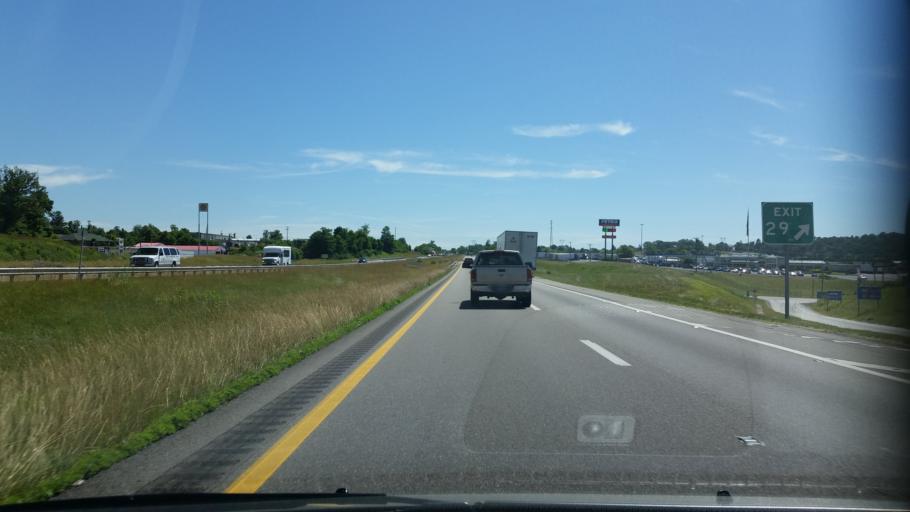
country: US
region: Virginia
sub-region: Washington County
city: Glade Spring
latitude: 36.7713
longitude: -81.7836
